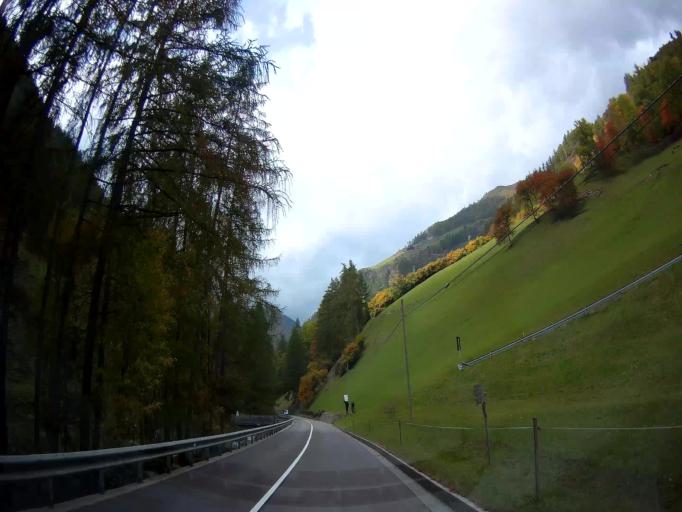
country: IT
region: Trentino-Alto Adige
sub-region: Bolzano
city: Senales
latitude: 46.7129
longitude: 10.8934
